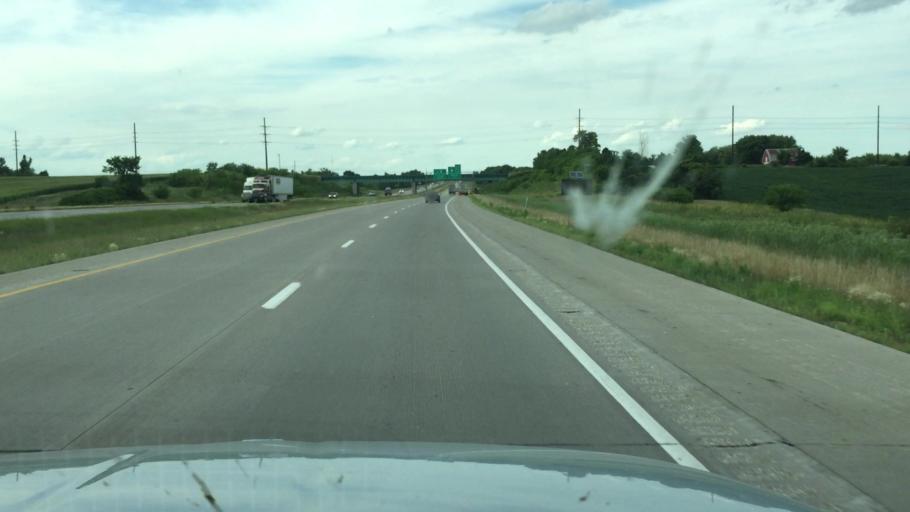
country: US
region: Iowa
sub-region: Scott County
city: Walcott
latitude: 41.5678
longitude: -90.6787
